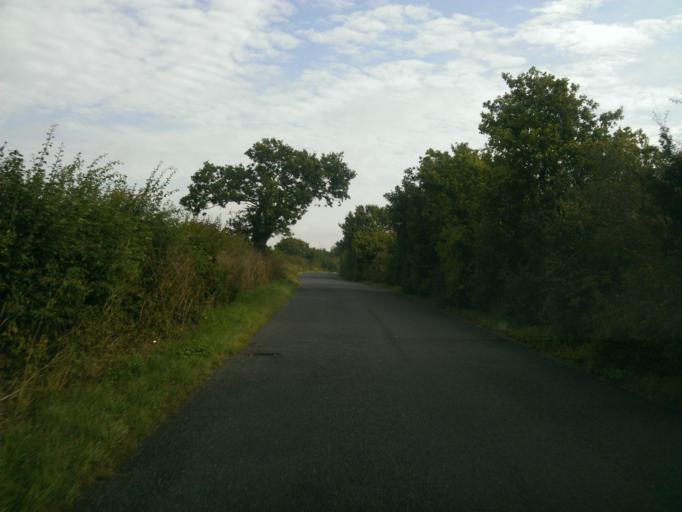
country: GB
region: England
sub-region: Essex
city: Saint Osyth
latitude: 51.8144
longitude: 1.0936
